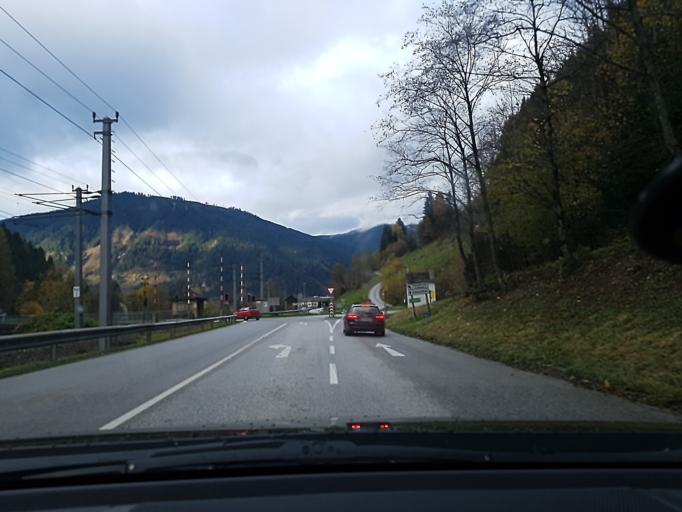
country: AT
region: Styria
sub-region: Politischer Bezirk Liezen
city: Selzthal
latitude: 47.5430
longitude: 14.3073
